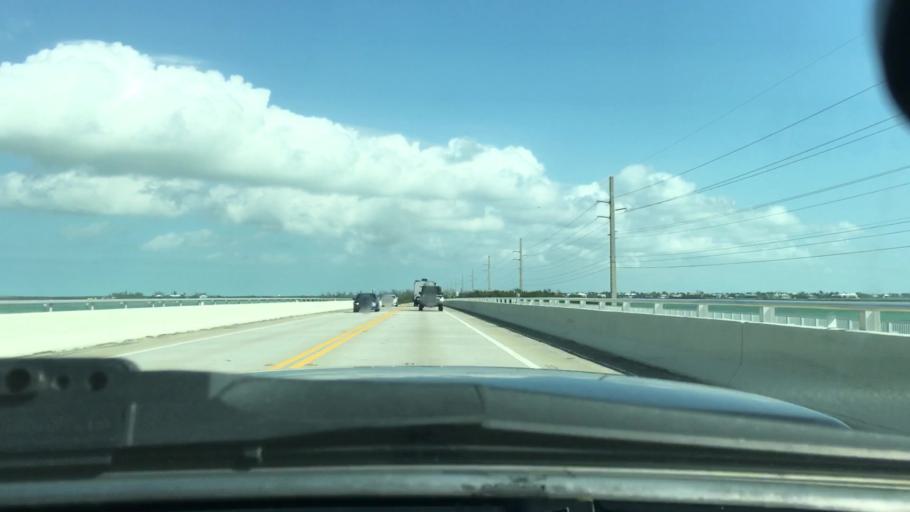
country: US
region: Florida
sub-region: Monroe County
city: Big Coppitt Key
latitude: 24.6335
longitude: -81.5870
